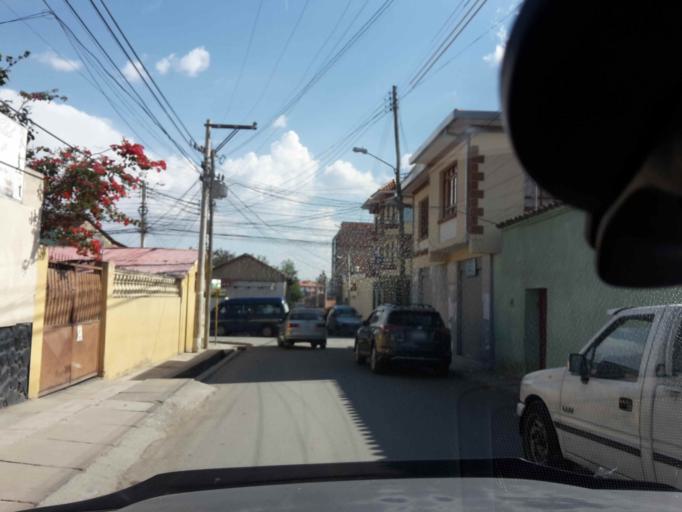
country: BO
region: Cochabamba
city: Cochabamba
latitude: -17.3385
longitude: -66.2199
